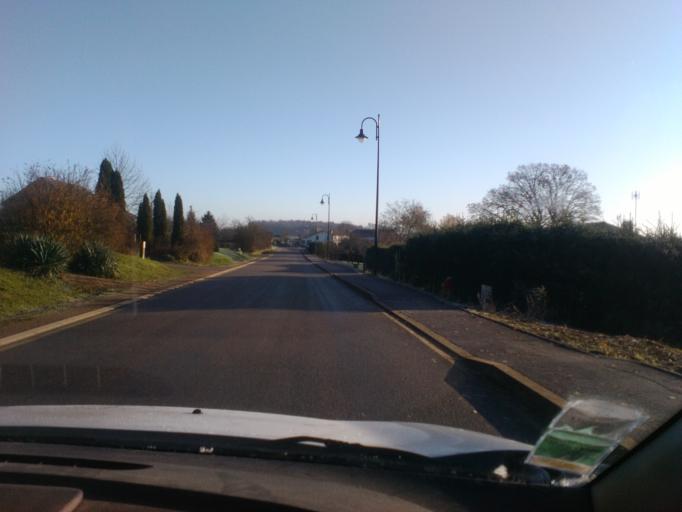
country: FR
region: Lorraine
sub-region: Departement des Vosges
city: Darnieulles
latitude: 48.1474
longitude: 6.2460
